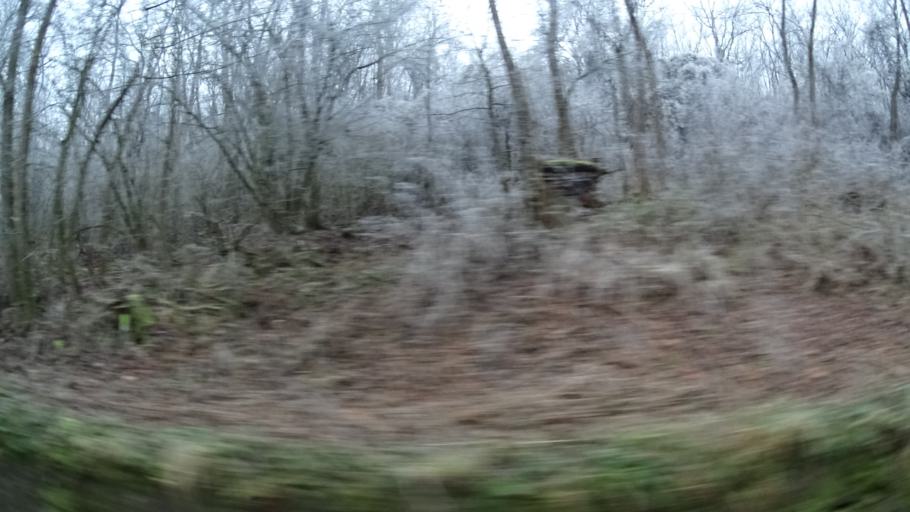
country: DE
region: Bavaria
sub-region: Regierungsbezirk Unterfranken
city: Marktsteft
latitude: 49.6847
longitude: 10.1361
